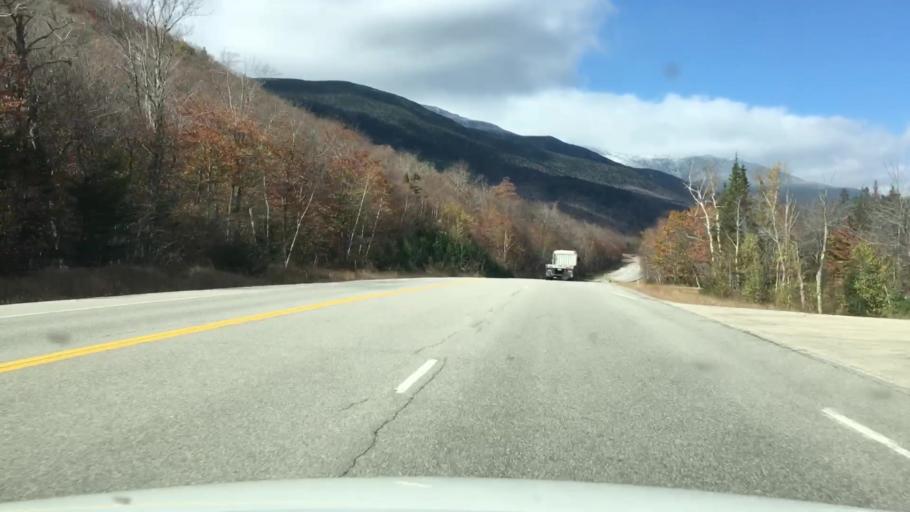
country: US
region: New Hampshire
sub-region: Coos County
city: Gorham
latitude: 44.2137
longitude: -71.2457
